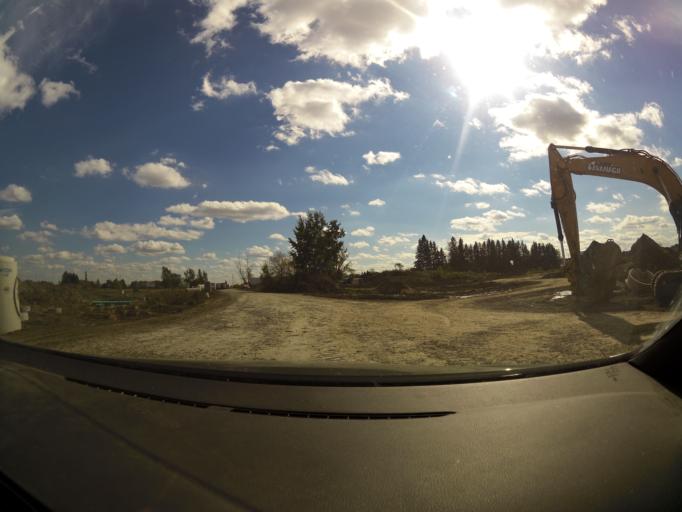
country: CA
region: Ontario
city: Bells Corners
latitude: 45.2710
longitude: -75.8815
